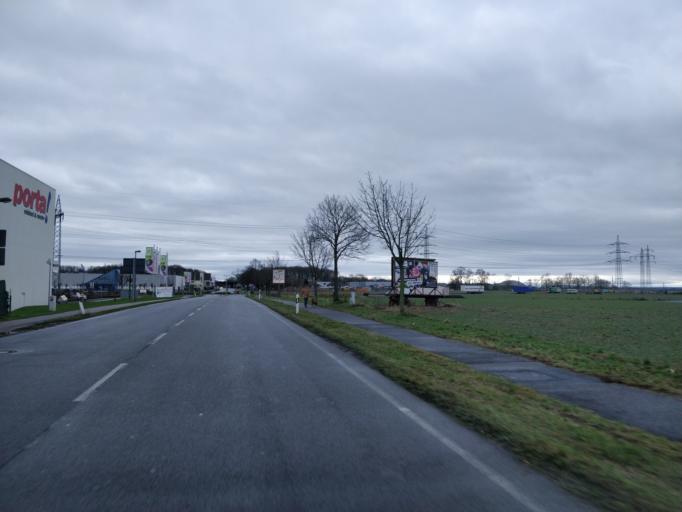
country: DE
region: North Rhine-Westphalia
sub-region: Regierungsbezirk Koln
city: Wahn-Heide
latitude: 50.8494
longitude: 7.0923
